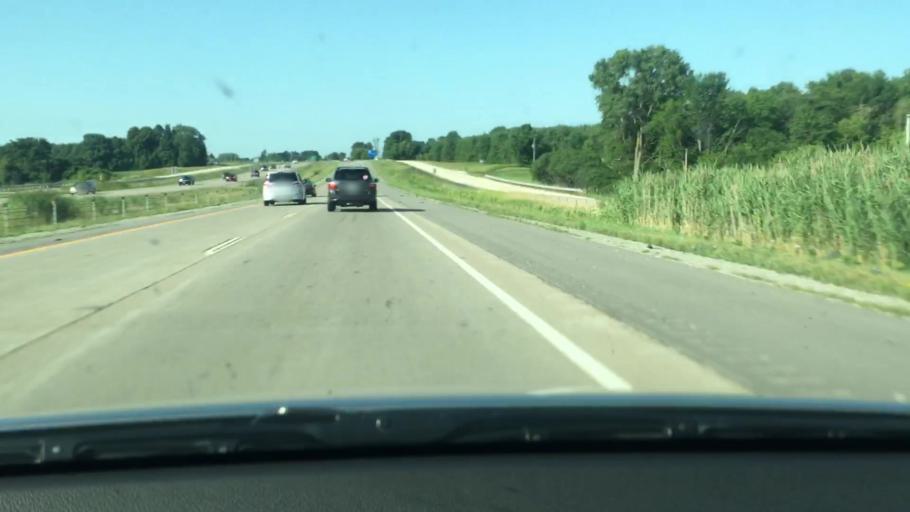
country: US
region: Wisconsin
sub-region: Brown County
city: Wrightstown
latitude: 44.3959
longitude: -88.1553
